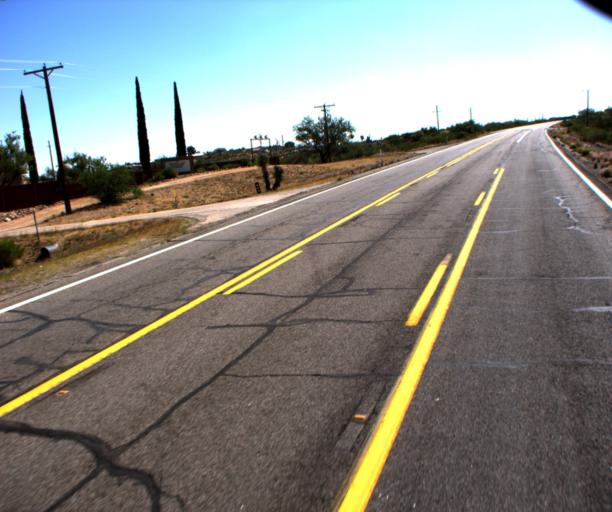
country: US
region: Arizona
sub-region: Pinal County
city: Oracle
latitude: 32.6218
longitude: -110.7974
